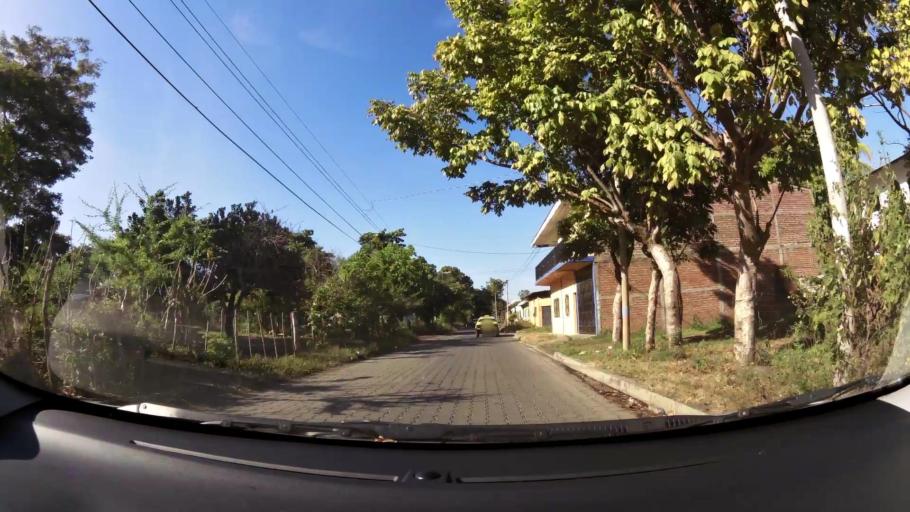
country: SV
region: San Miguel
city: San Miguel
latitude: 13.4784
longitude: -88.1934
